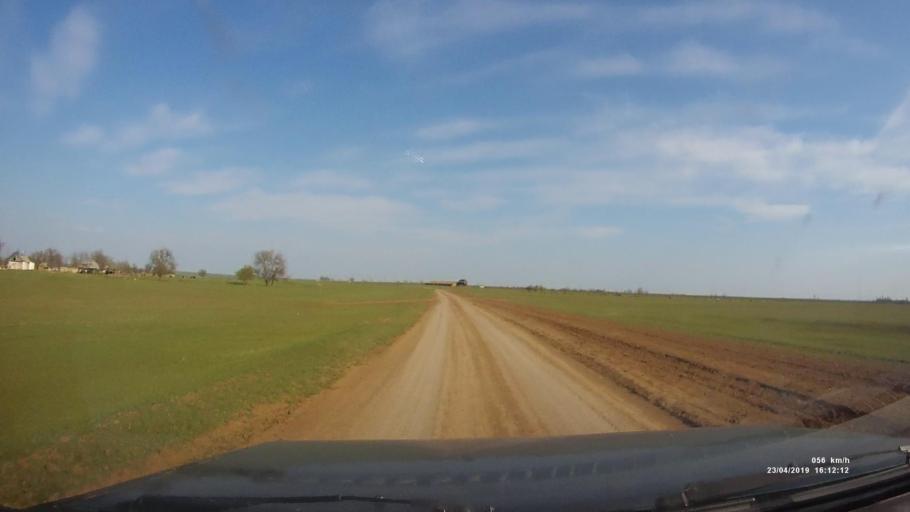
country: RU
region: Kalmykiya
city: Priyutnoye
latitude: 46.4677
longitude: 43.1241
